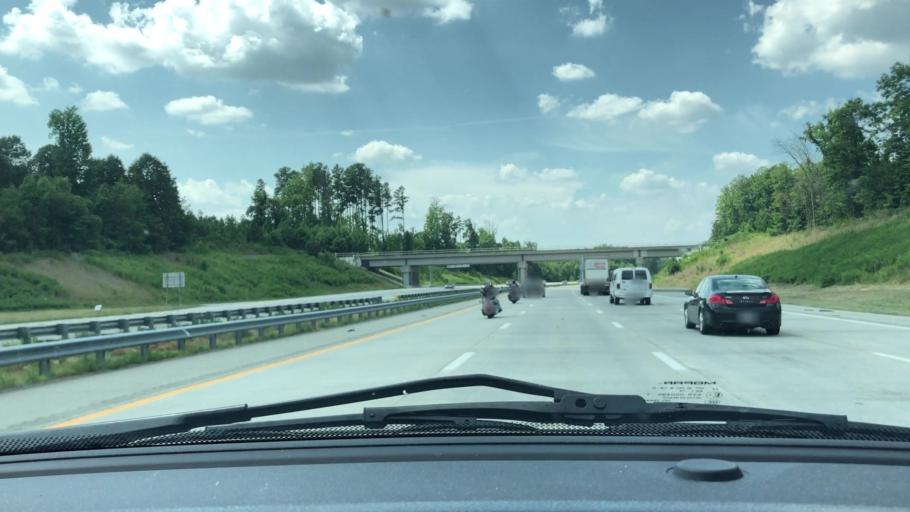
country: US
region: North Carolina
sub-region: Guilford County
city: Jamestown
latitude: 36.0279
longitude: -79.8845
